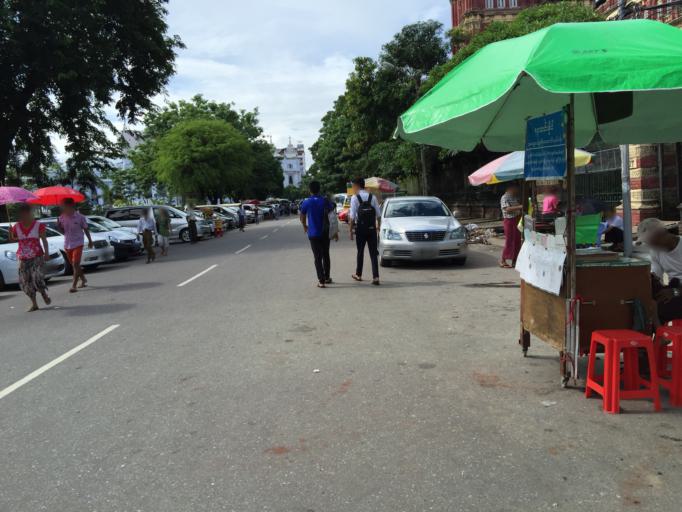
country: MM
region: Yangon
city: Yangon
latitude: 16.7726
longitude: 96.1604
